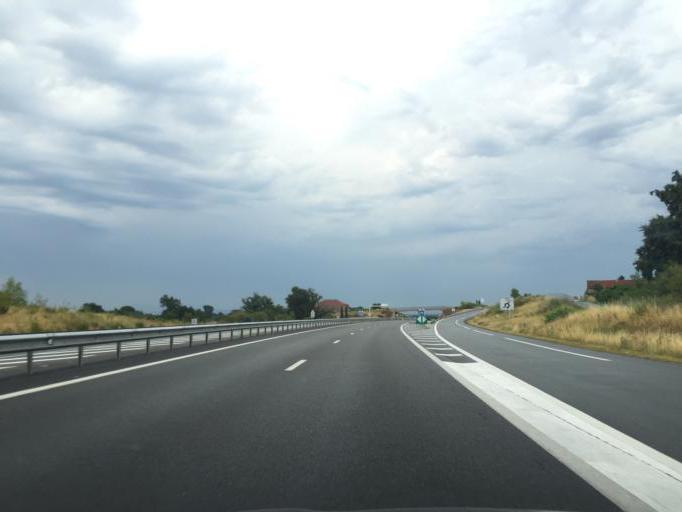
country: FR
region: Rhone-Alpes
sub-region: Departement de la Loire
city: La Pacaudiere
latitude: 46.1916
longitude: 3.8569
